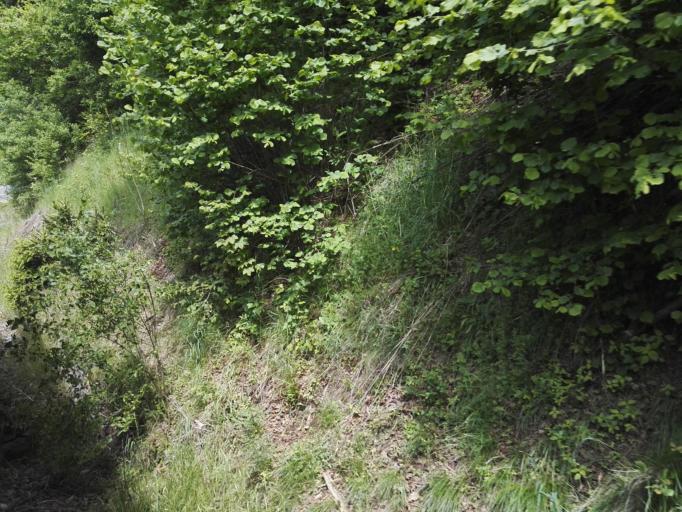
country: AT
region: Styria
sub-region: Politischer Bezirk Weiz
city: Koglhof
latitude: 47.2987
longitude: 15.6919
